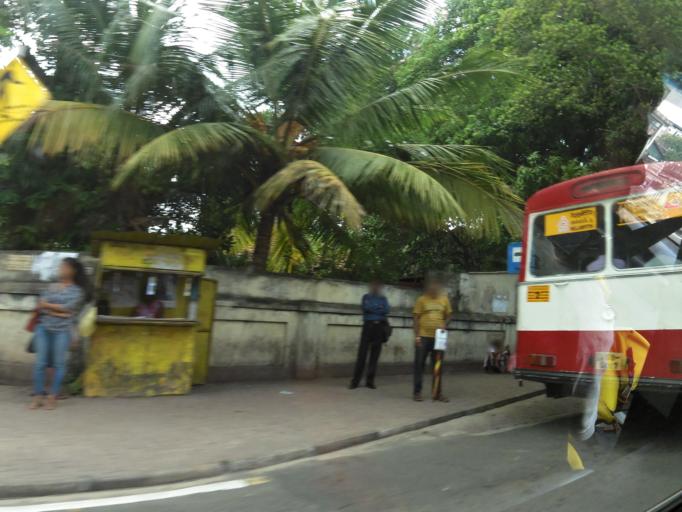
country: LK
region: Western
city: Kolonnawa
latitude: 6.9317
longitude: 79.8781
